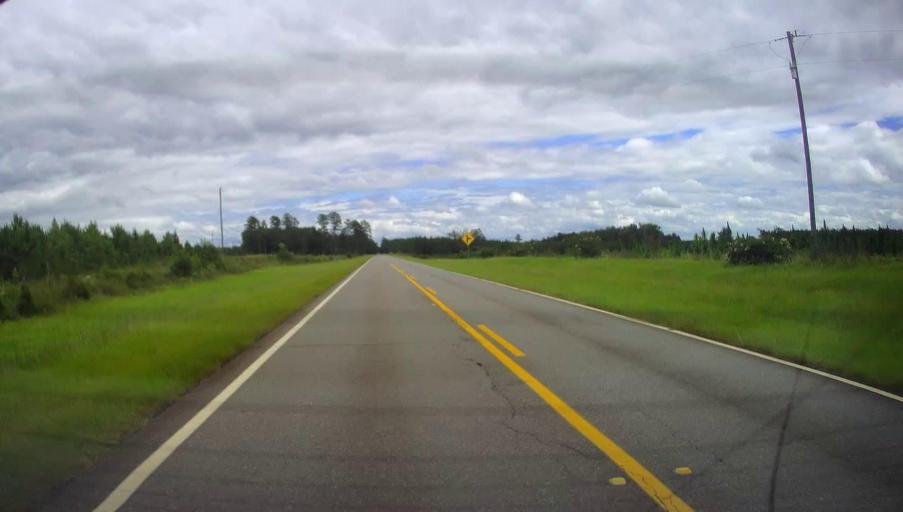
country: US
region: Georgia
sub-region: Twiggs County
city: Jeffersonville
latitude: 32.6804
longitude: -83.3095
